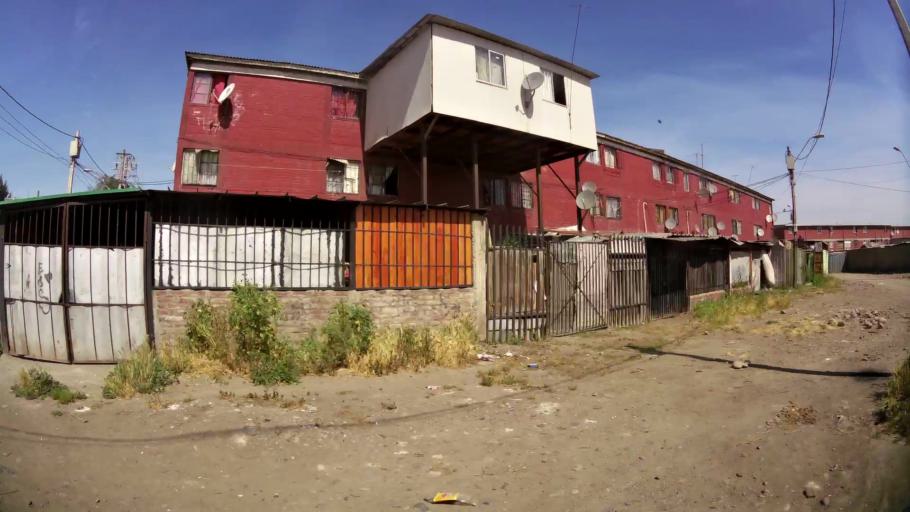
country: CL
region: Santiago Metropolitan
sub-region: Provincia de Maipo
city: San Bernardo
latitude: -33.5221
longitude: -70.7020
